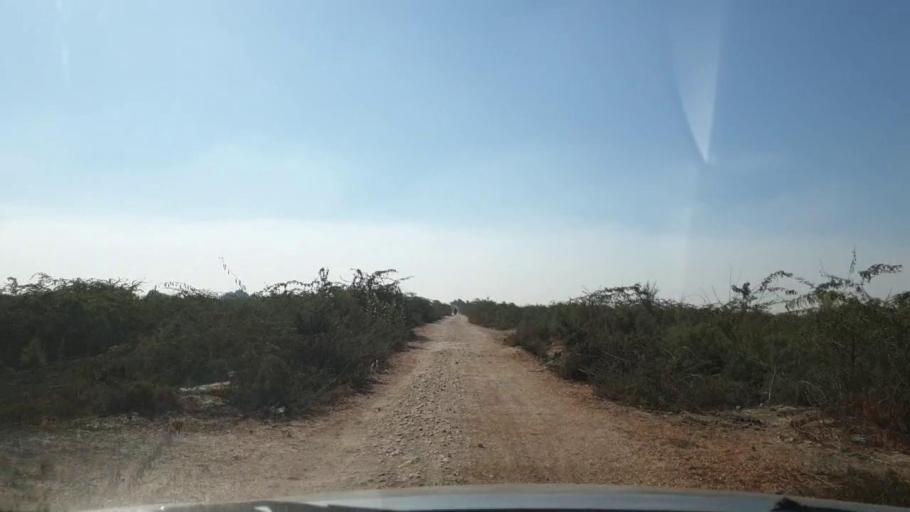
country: PK
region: Sindh
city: Jhol
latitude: 25.8162
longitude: 69.0117
